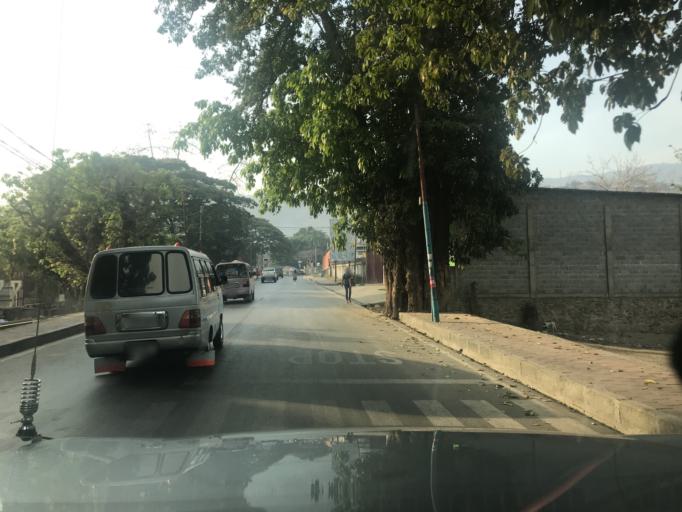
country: TL
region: Dili
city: Dili
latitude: -8.5640
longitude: 125.5813
